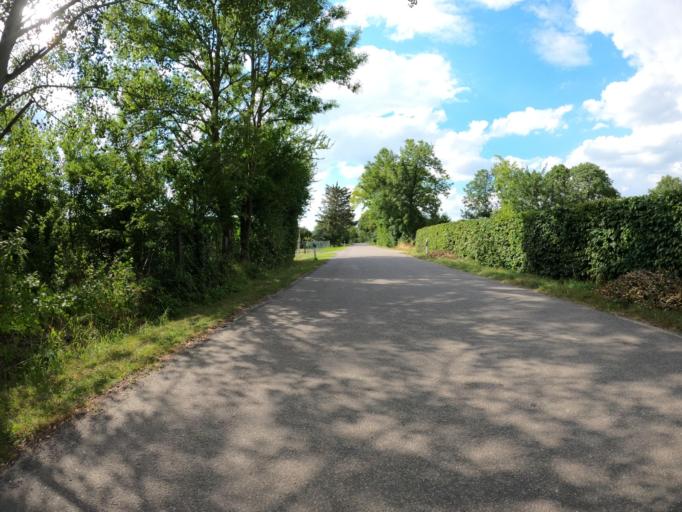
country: DE
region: Mecklenburg-Vorpommern
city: Woldegk
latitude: 53.4369
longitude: 13.5985
